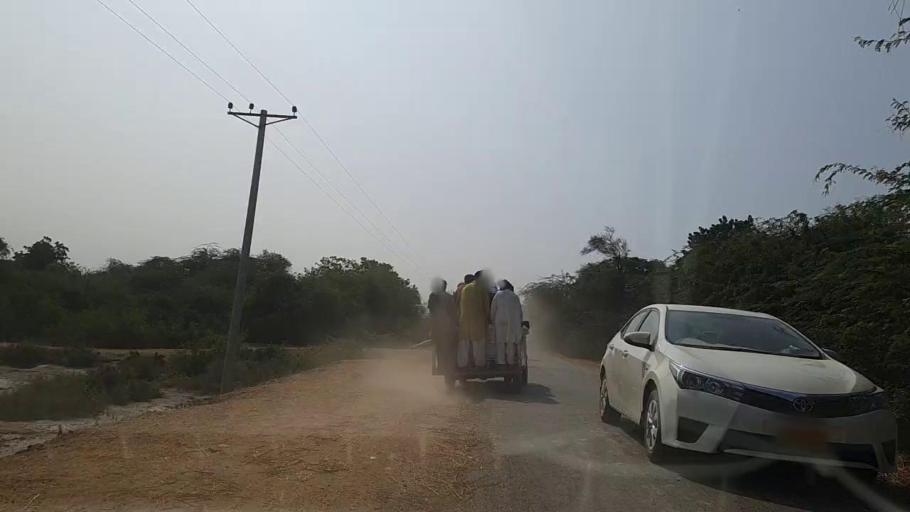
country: PK
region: Sindh
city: Chuhar Jamali
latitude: 24.3682
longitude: 67.9651
